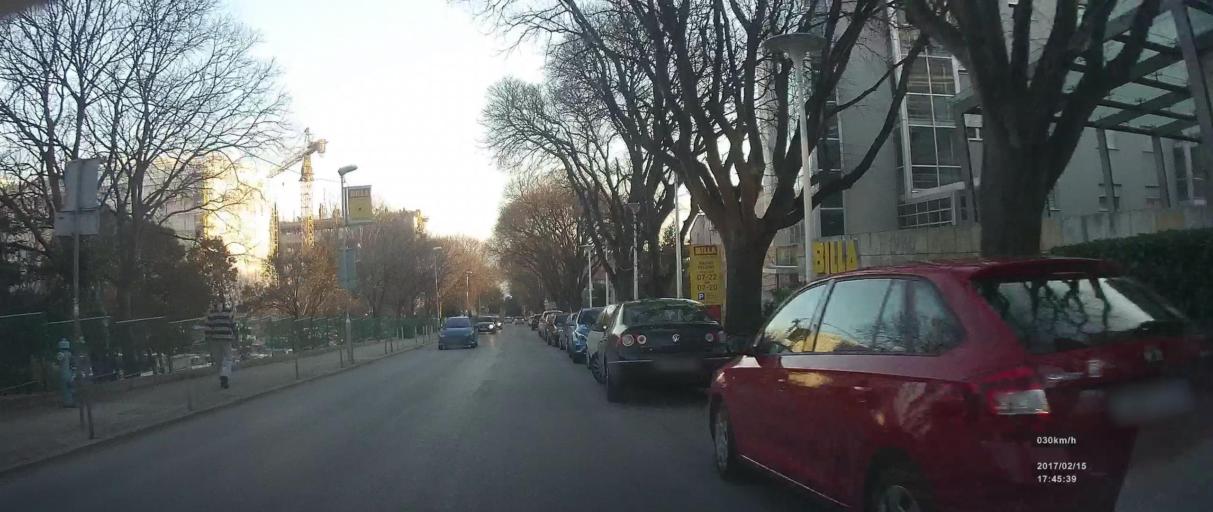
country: HR
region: Splitsko-Dalmatinska
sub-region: Grad Split
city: Split
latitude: 43.5041
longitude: 16.4565
